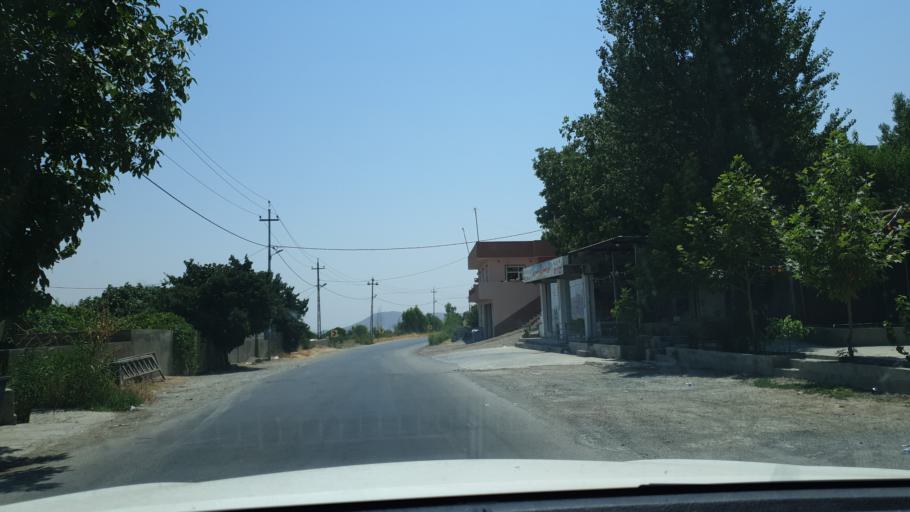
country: IQ
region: Arbil
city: Nahiyat Hiran
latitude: 36.2928
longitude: 44.4769
